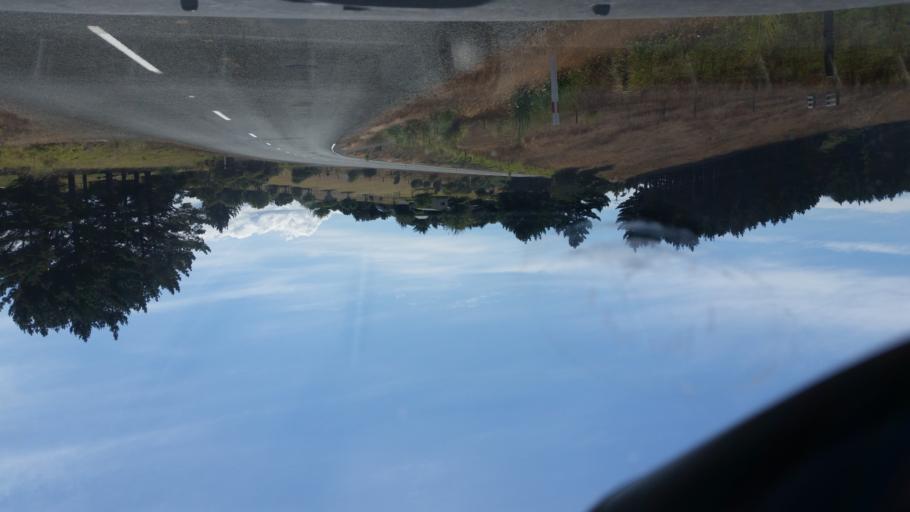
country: NZ
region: Auckland
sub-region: Auckland
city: Wellsford
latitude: -36.1943
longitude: 174.1621
